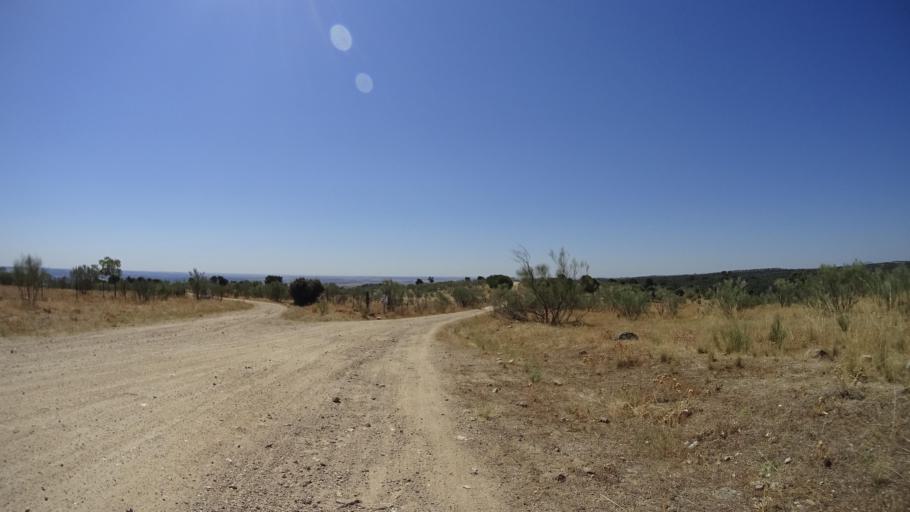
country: ES
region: Madrid
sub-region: Provincia de Madrid
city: Colmenarejo
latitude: 40.5149
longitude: -4.0141
